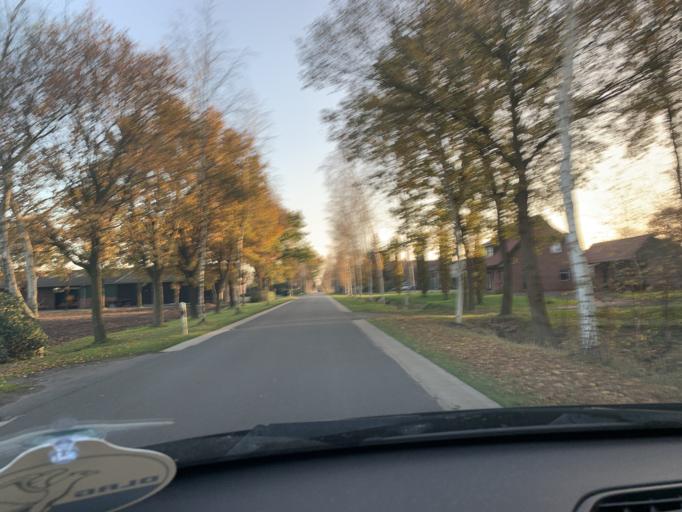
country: DE
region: Lower Saxony
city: Bad Zwischenahn
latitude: 53.1527
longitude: 8.0520
